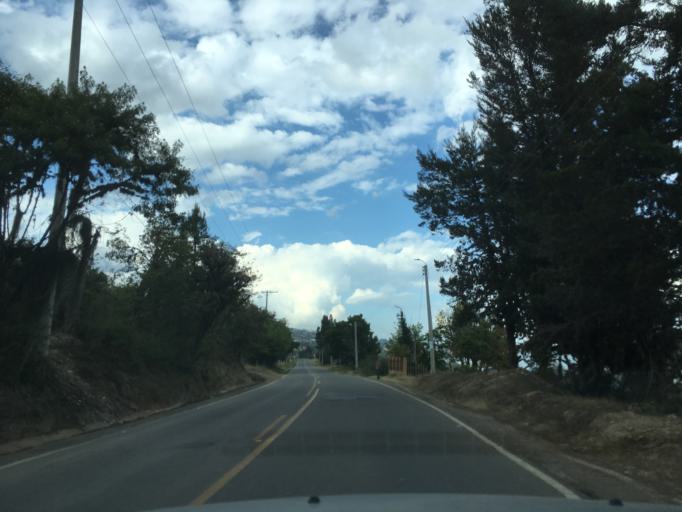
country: CO
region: Boyaca
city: Sutamarchan
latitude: 5.5903
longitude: -73.6399
